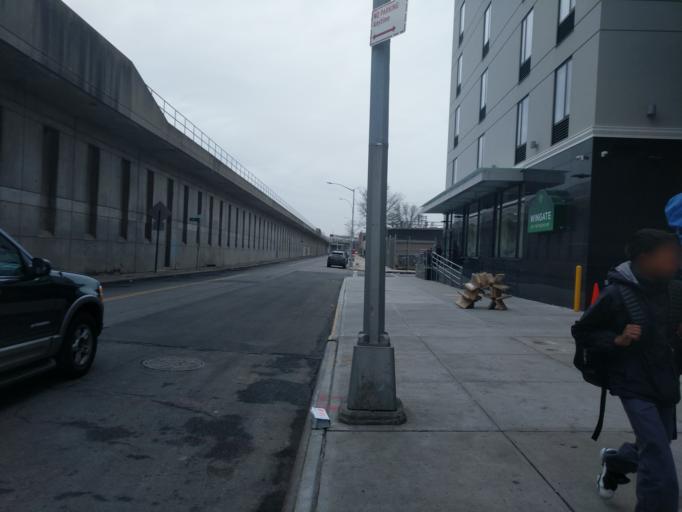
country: US
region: New York
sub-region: Queens County
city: Jamaica
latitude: 40.6995
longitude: -73.8111
